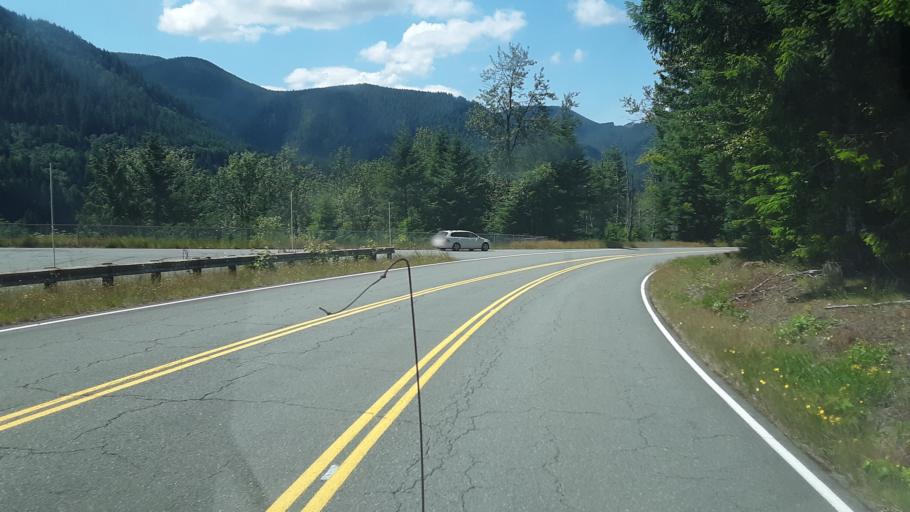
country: US
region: Washington
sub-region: Clark County
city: Yacolt
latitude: 46.0666
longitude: -122.1999
